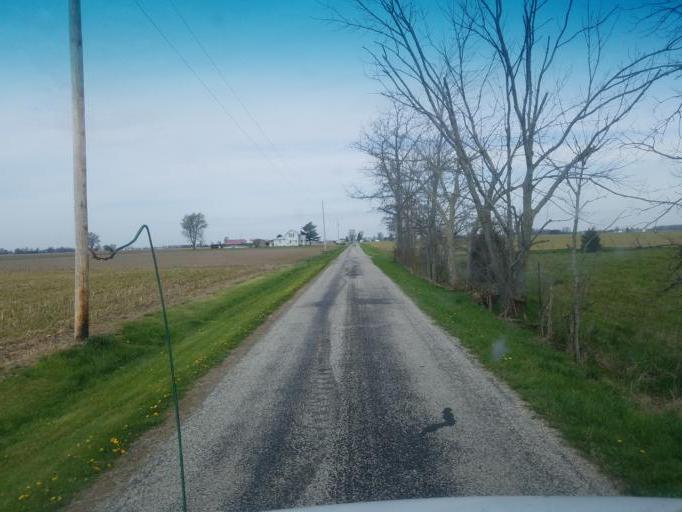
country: US
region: Ohio
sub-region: Marion County
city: Prospect
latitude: 40.4333
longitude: -83.2255
